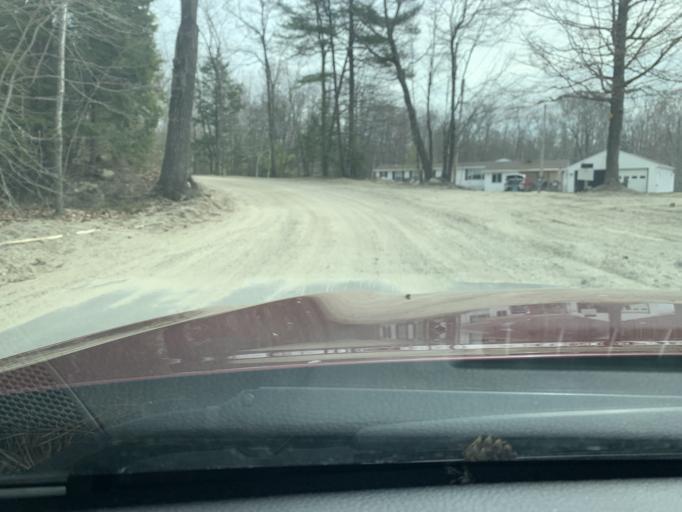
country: US
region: Maine
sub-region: Androscoggin County
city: Poland
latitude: 43.9665
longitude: -70.3828
